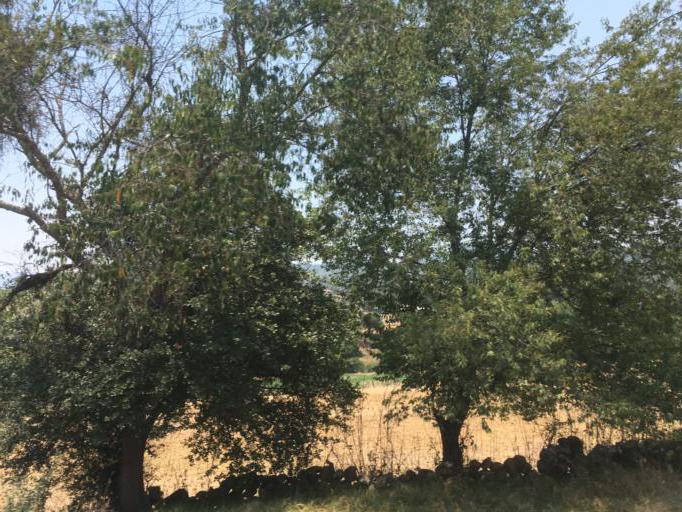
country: MX
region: Michoacan
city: Quiroga
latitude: 19.6363
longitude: -101.4748
